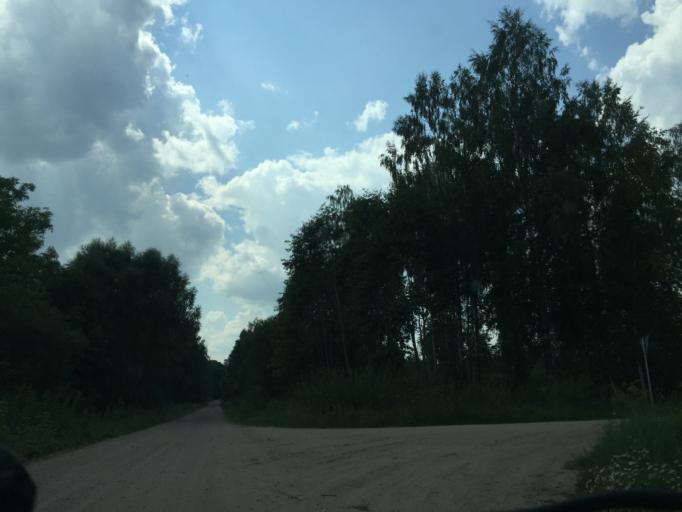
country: LT
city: Zagare
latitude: 56.3770
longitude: 23.1719
